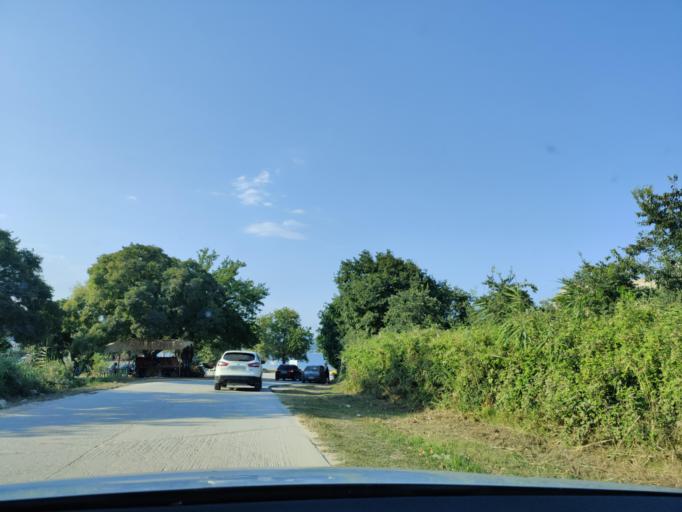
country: GR
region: East Macedonia and Thrace
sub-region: Nomos Kavalas
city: Nea Peramos
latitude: 40.8251
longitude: 24.3074
